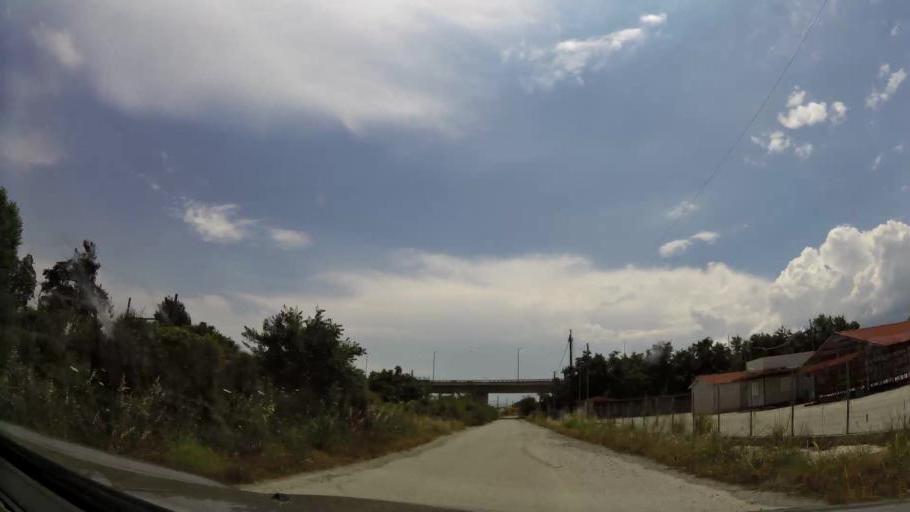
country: GR
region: Central Macedonia
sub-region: Nomos Pierias
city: Peristasi
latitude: 40.2643
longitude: 22.5300
